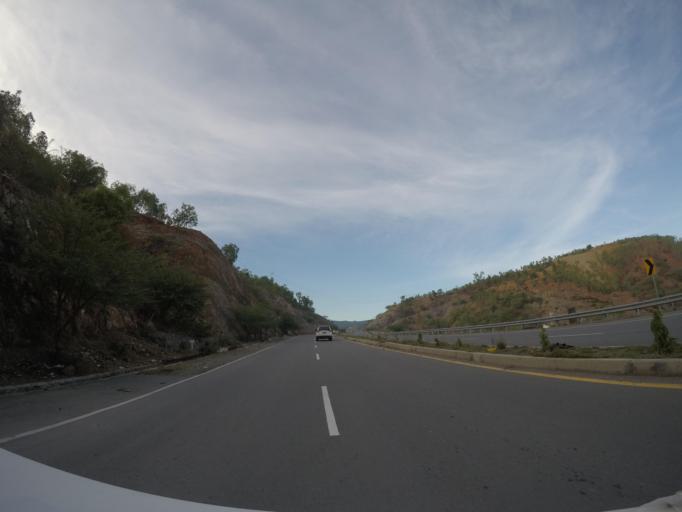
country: TL
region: Dili
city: Dili
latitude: -8.5597
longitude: 125.4946
